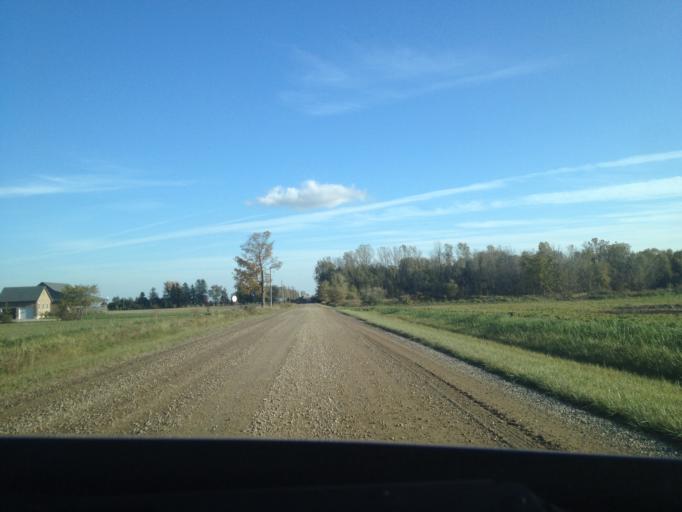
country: CA
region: Ontario
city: Delaware
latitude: 42.6584
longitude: -81.5562
